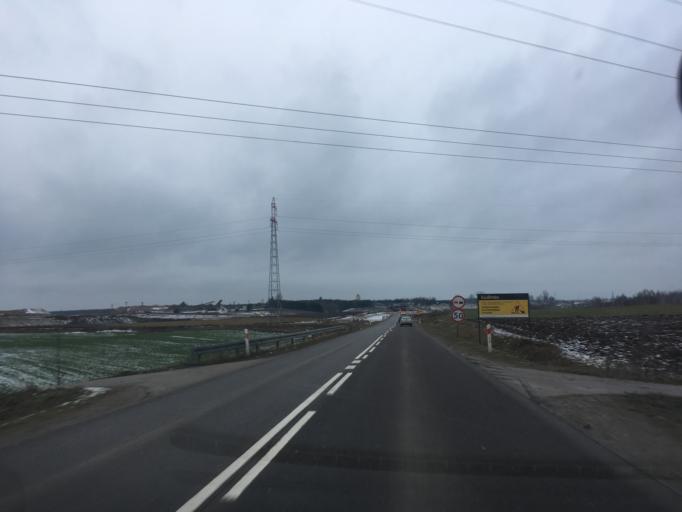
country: PL
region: Podlasie
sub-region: Suwalki
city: Suwalki
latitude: 54.1069
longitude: 22.8821
